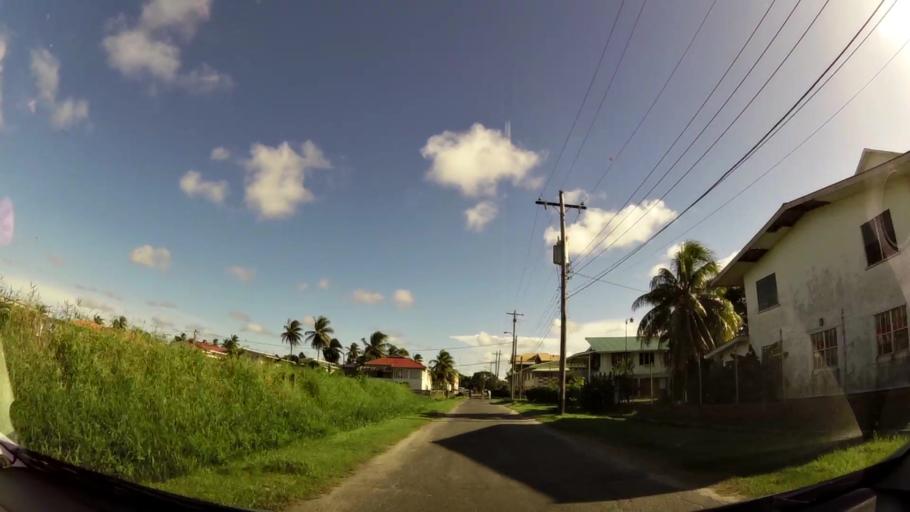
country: GY
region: Demerara-Mahaica
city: Georgetown
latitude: 6.8233
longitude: -58.1356
